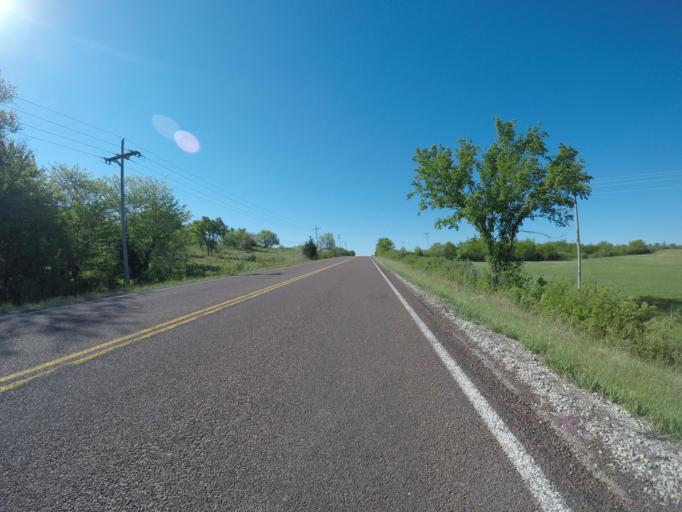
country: US
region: Kansas
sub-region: Douglas County
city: Lawrence
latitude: 38.9974
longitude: -95.3913
